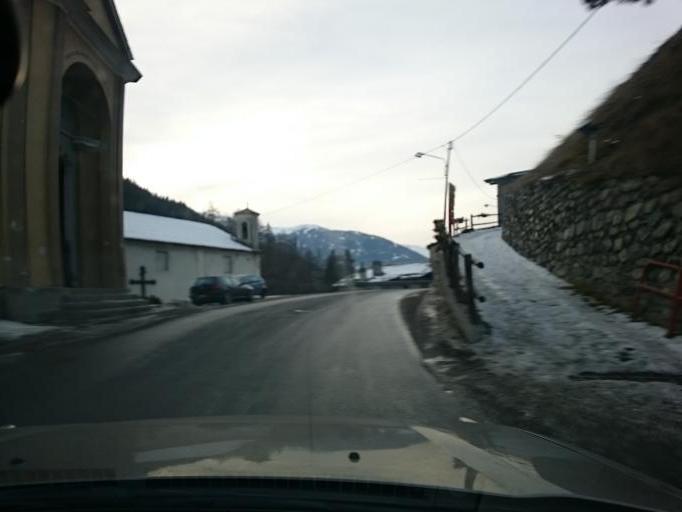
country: IT
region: Lombardy
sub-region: Provincia di Sondrio
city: San Nicolo
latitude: 46.4628
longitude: 10.4083
